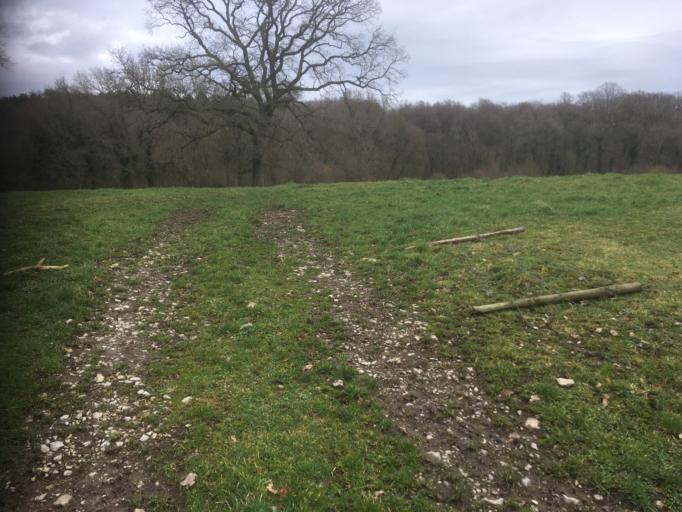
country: BE
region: Wallonia
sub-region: Province du Luxembourg
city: Durbuy
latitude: 50.3056
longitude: 5.4917
